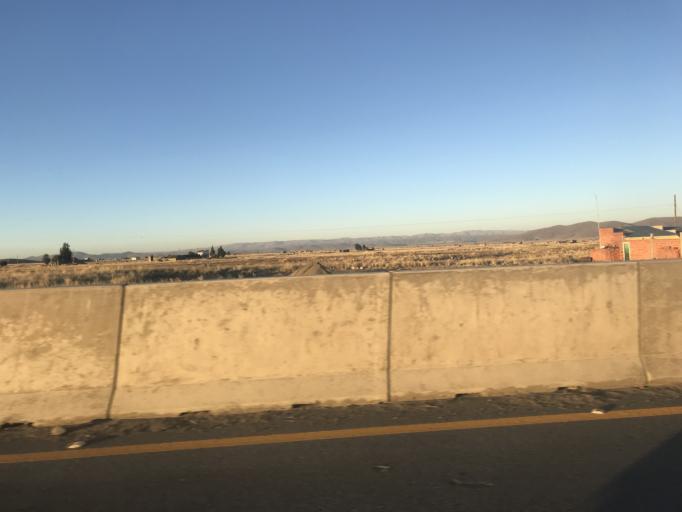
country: BO
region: La Paz
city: Batallas
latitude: -16.3061
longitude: -68.4758
